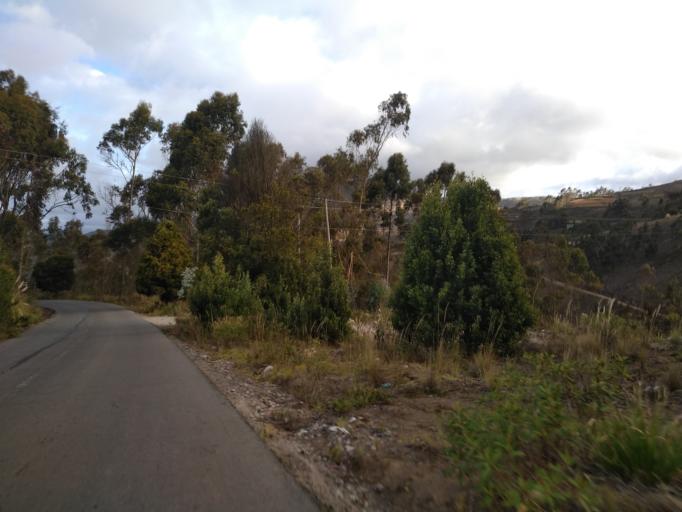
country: EC
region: Chimborazo
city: Riobamba
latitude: -1.7019
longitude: -78.7090
